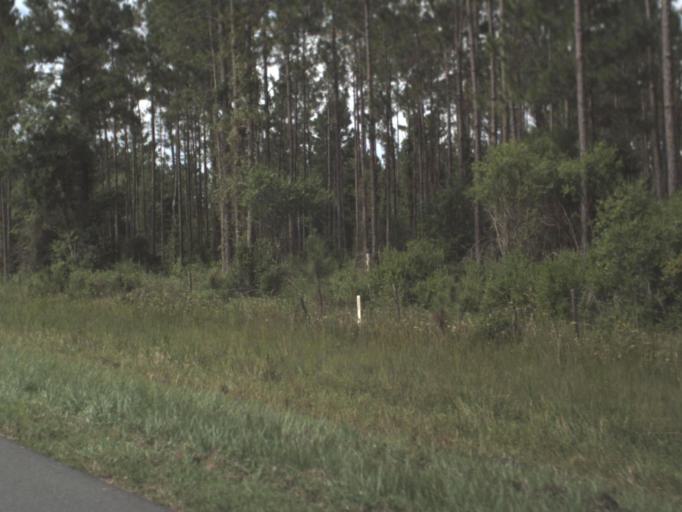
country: US
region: Florida
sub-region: Columbia County
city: Five Points
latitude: 30.3867
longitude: -82.6273
